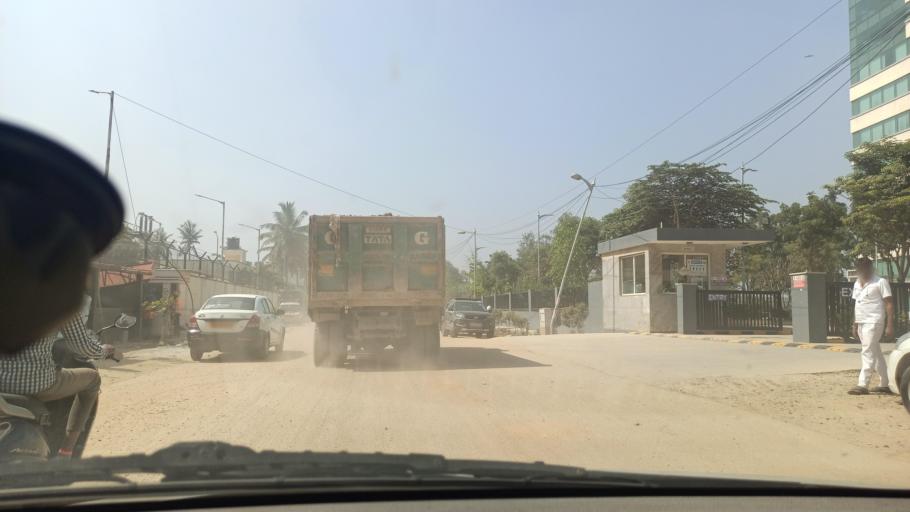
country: IN
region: Karnataka
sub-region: Bangalore Urban
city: Bangalore
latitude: 12.9394
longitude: 77.6894
